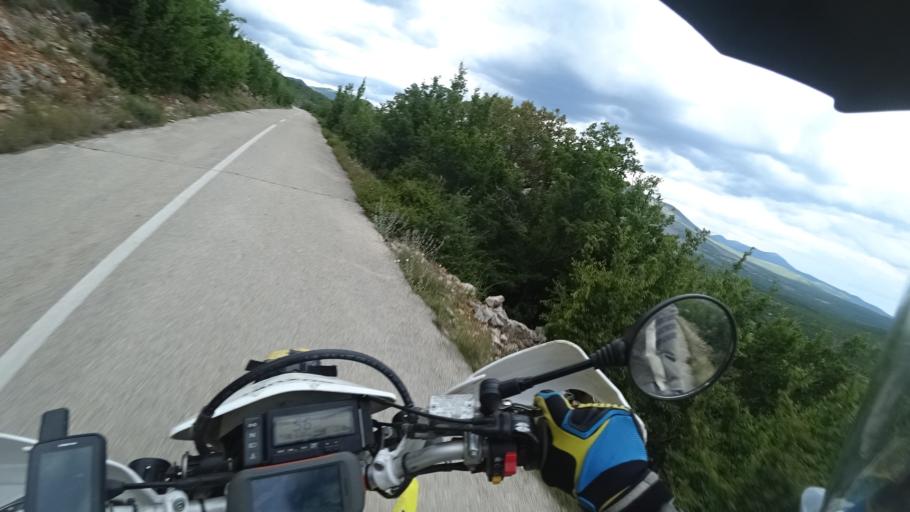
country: HR
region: Zadarska
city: Gracac
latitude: 44.1941
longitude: 15.8769
